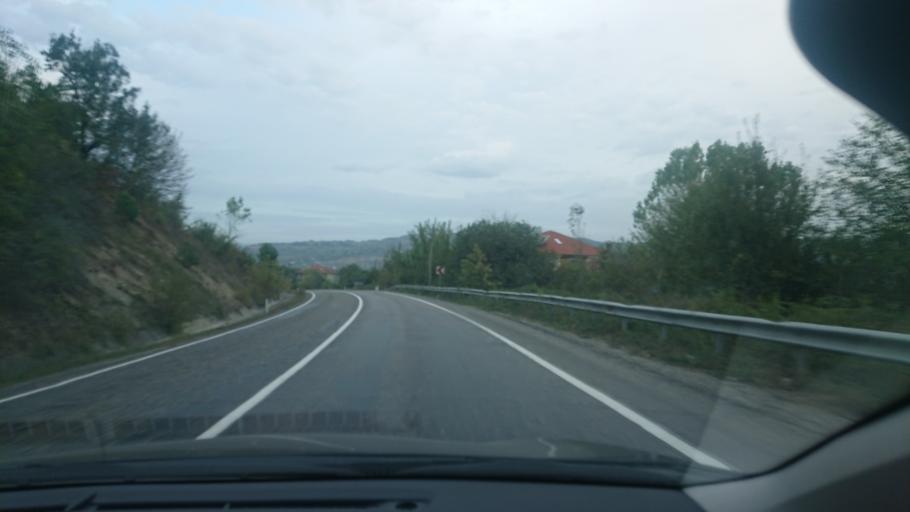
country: TR
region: Zonguldak
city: Gokcebey
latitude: 41.2885
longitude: 32.1404
